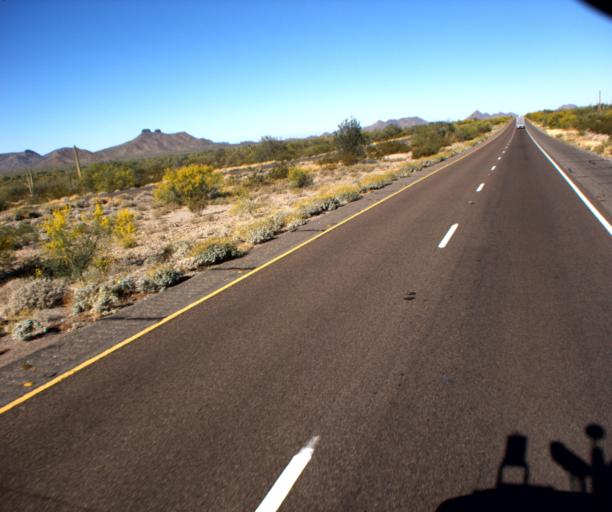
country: US
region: Arizona
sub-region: Maricopa County
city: Gila Bend
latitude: 32.8649
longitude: -112.4117
